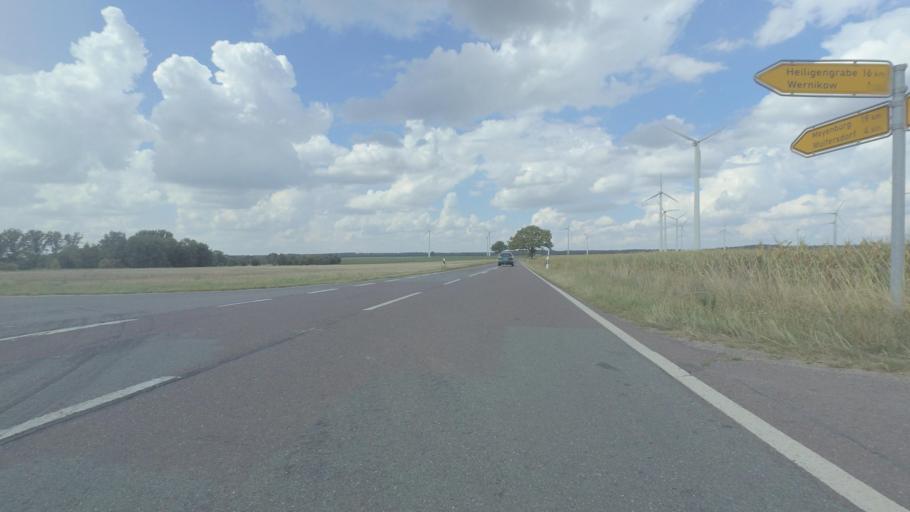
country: DE
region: Brandenburg
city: Wittstock
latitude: 53.2079
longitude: 12.4436
